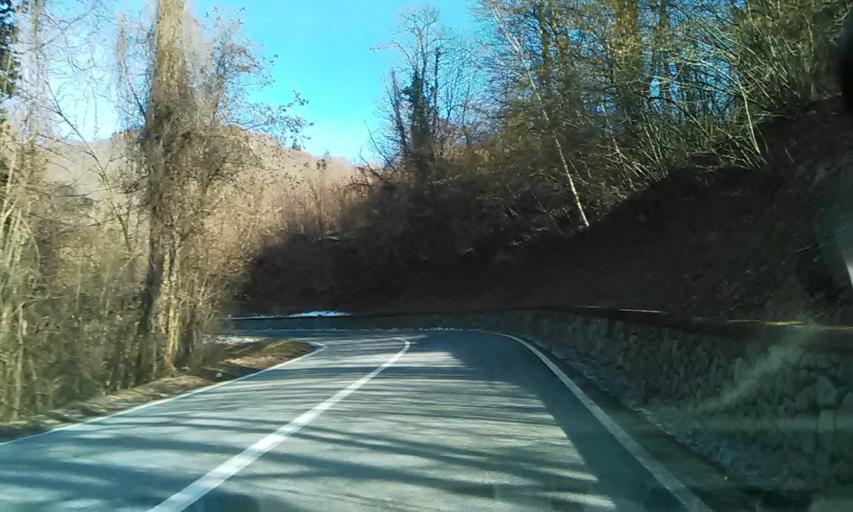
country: IT
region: Piedmont
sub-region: Provincia di Vercelli
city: Cellio
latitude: 45.7462
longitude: 8.3093
